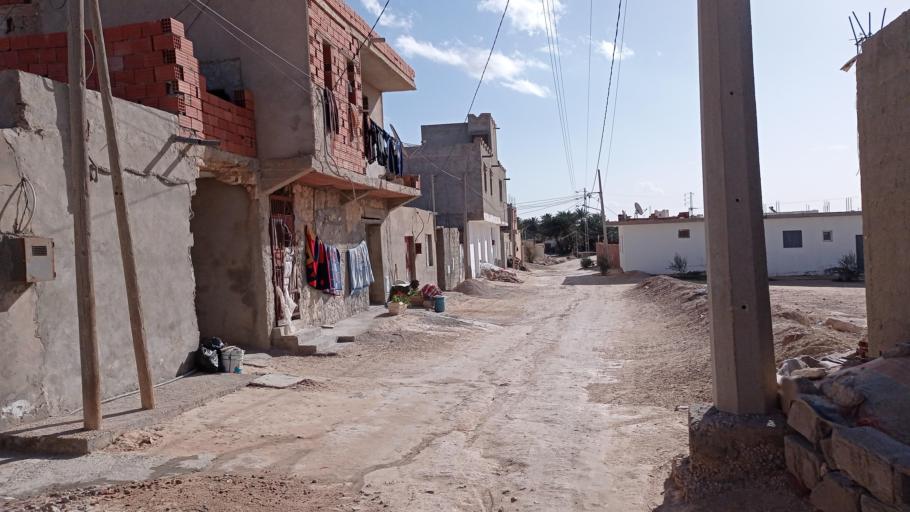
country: TN
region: Qabis
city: Gabes
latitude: 33.8344
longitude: 10.1094
